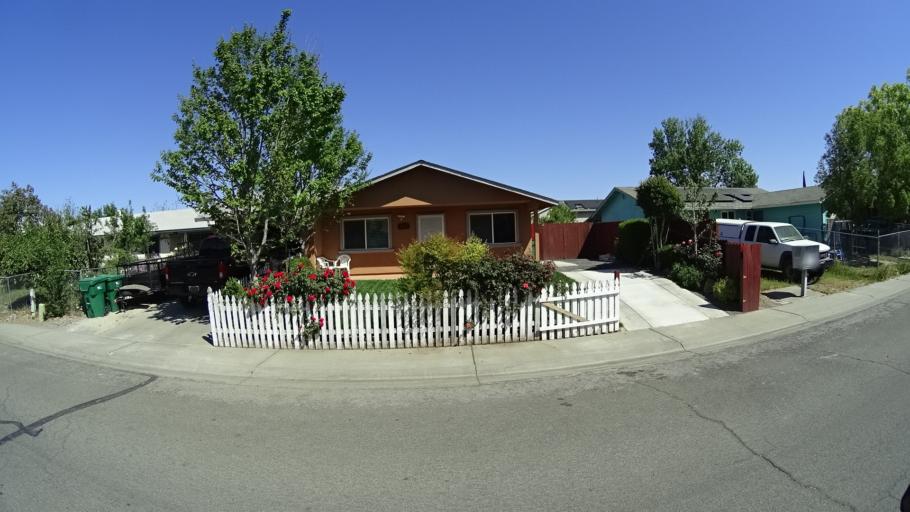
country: US
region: California
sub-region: Glenn County
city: Orland
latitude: 39.7570
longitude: -122.2007
